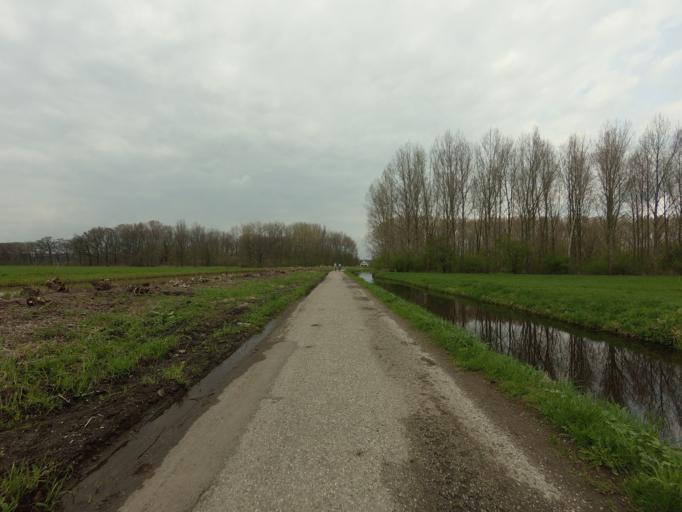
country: NL
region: Utrecht
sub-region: Stichtse Vecht
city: Breukelen
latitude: 52.1703
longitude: 5.0237
